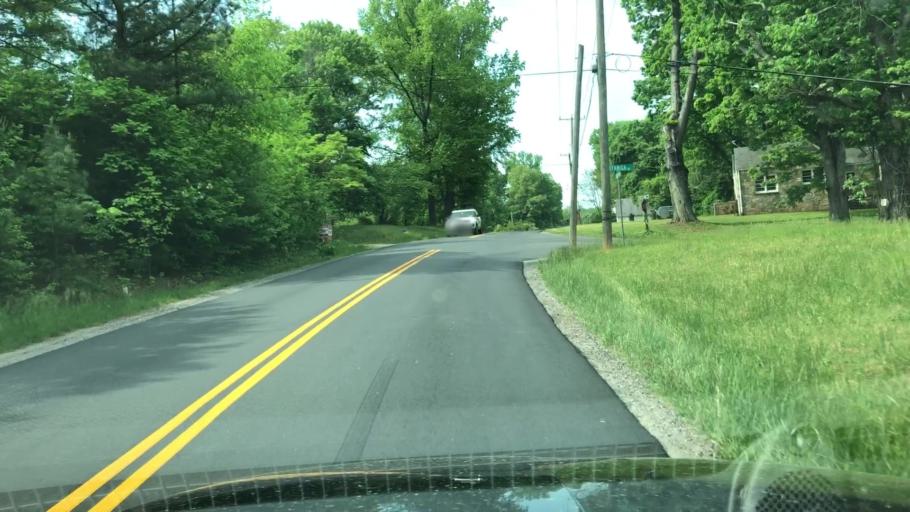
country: US
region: Virginia
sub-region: Stafford County
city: Stafford
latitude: 38.4456
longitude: -77.4887
